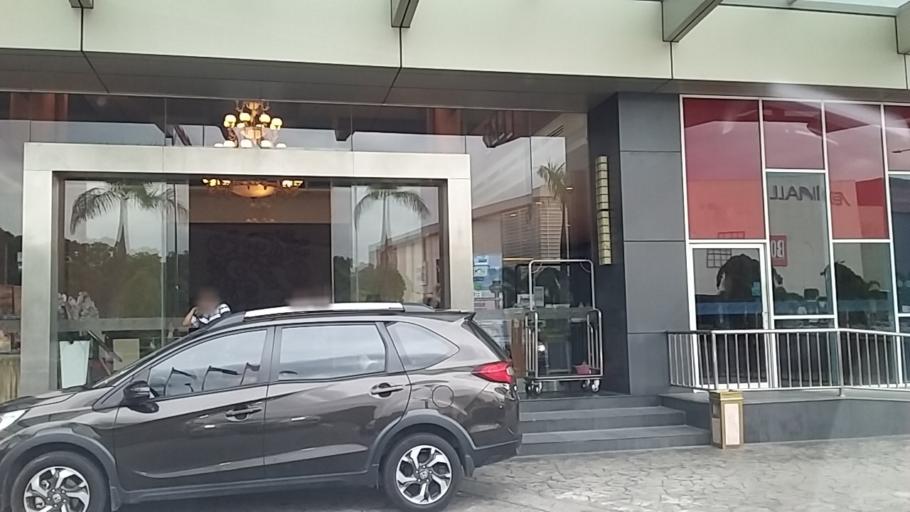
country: MY
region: Johor
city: Skudai
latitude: 1.4820
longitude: 103.6581
